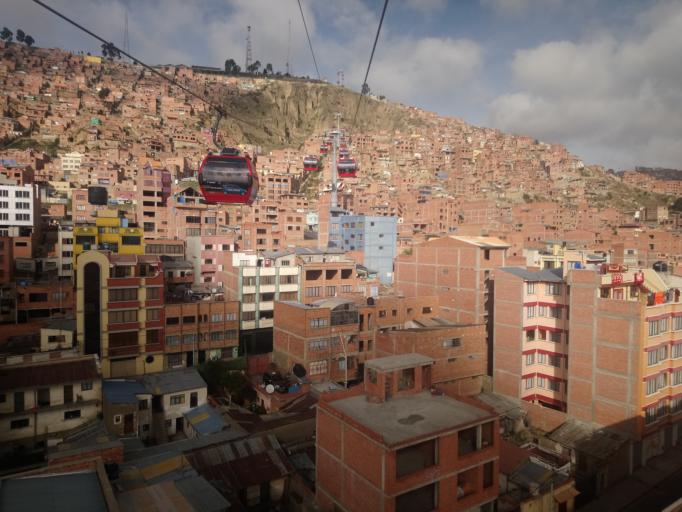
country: BO
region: La Paz
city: La Paz
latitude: -16.4979
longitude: -68.1568
